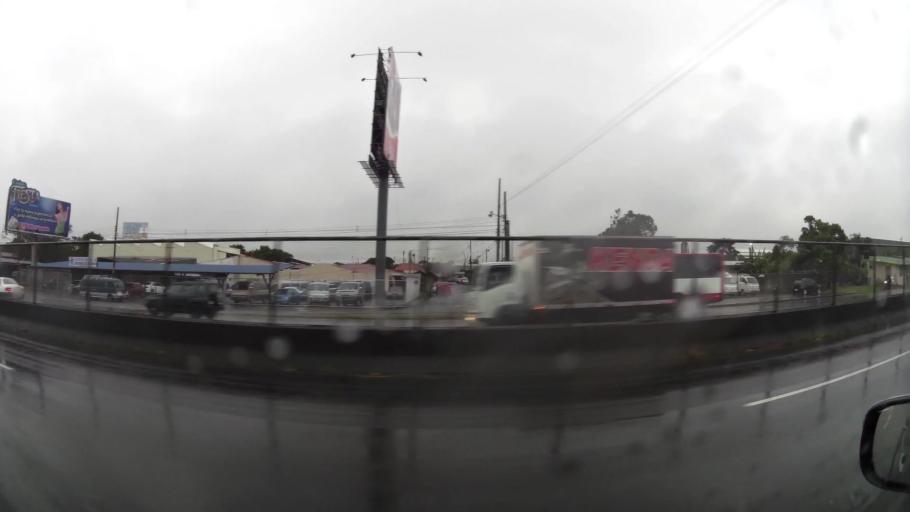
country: CR
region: Heredia
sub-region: Canton de Belen
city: San Antonio
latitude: 10.0007
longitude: -84.1863
